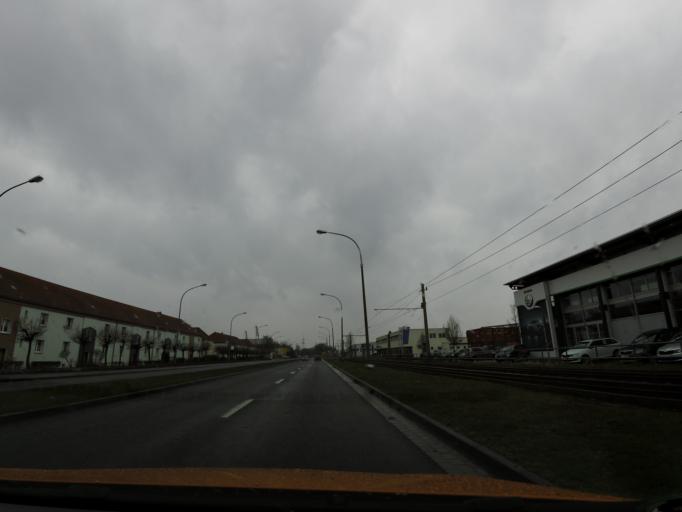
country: DE
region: Brandenburg
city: Brandenburg an der Havel
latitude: 52.4140
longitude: 12.5097
